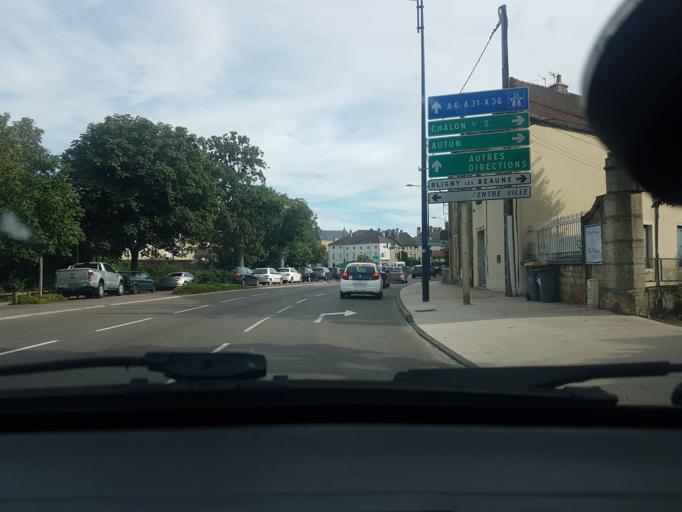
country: FR
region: Bourgogne
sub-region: Departement de la Cote-d'Or
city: Beaune
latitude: 47.0232
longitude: 4.8330
